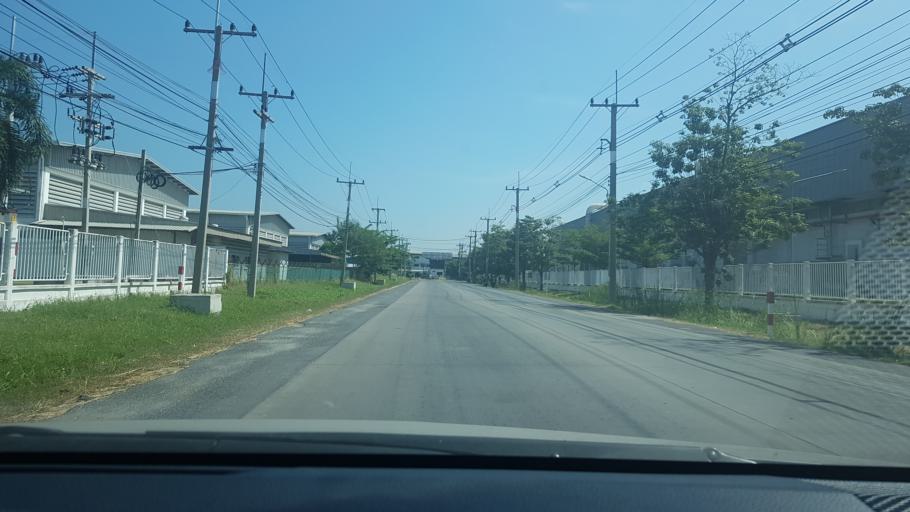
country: TH
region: Phra Nakhon Si Ayutthaya
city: Bang Pa-in
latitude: 14.2474
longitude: 100.5978
